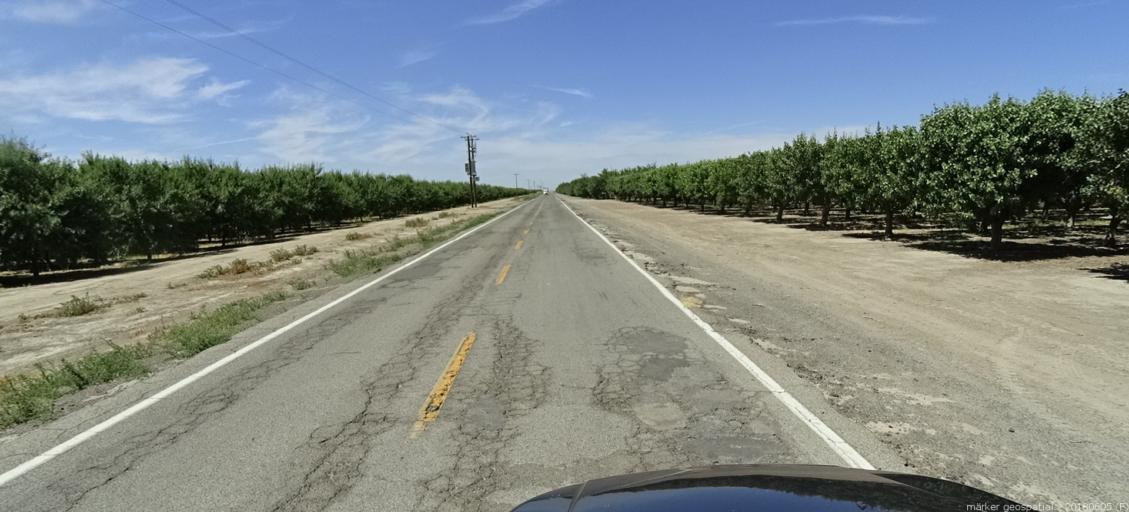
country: US
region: California
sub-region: Fresno County
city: Firebaugh
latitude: 36.9658
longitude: -120.3828
